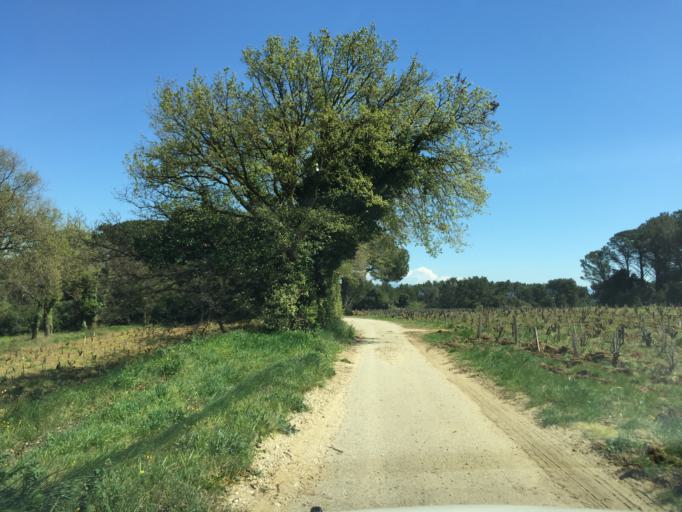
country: FR
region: Provence-Alpes-Cote d'Azur
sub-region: Departement du Vaucluse
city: Chateauneuf-du-Pape
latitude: 44.0801
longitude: 4.8448
